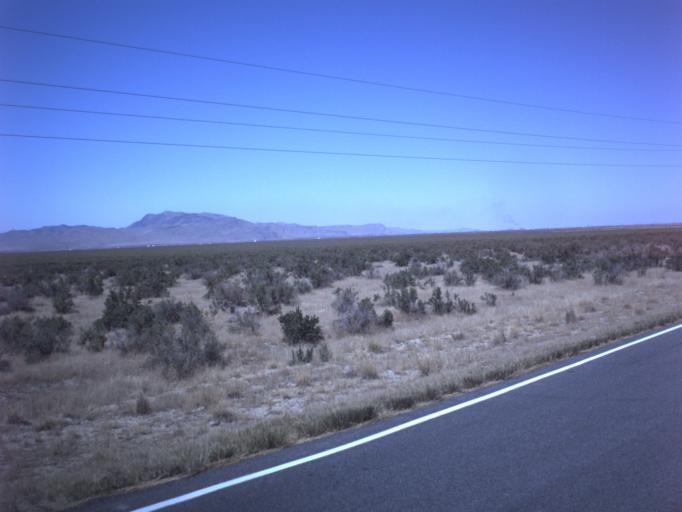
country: US
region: Utah
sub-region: Tooele County
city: Grantsville
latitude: 40.7059
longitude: -112.6643
